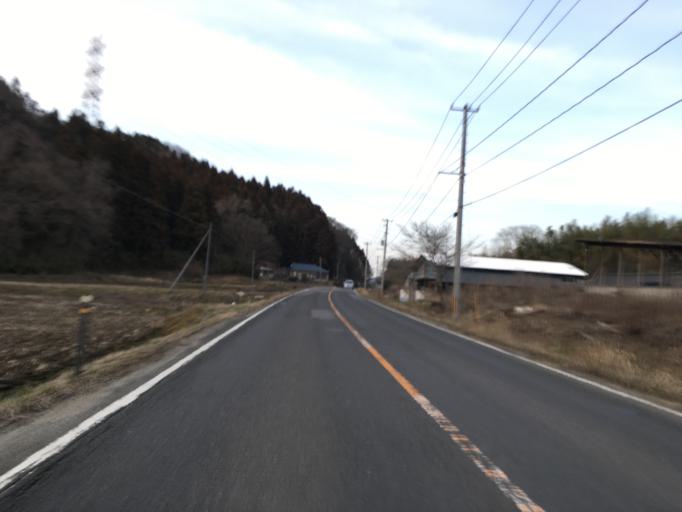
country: JP
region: Ibaraki
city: Daigo
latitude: 36.8895
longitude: 140.4112
